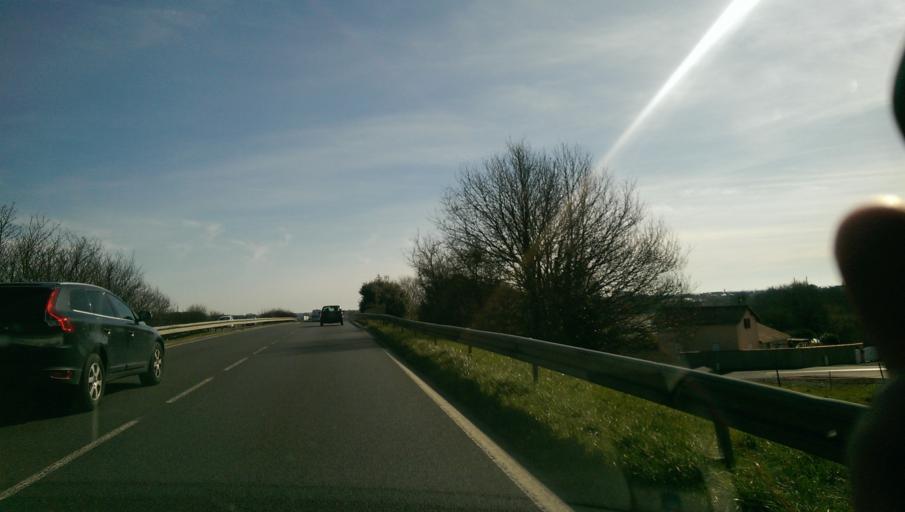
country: FR
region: Pays de la Loire
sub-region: Departement de Maine-et-Loire
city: Cholet
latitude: 47.0752
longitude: -0.8835
